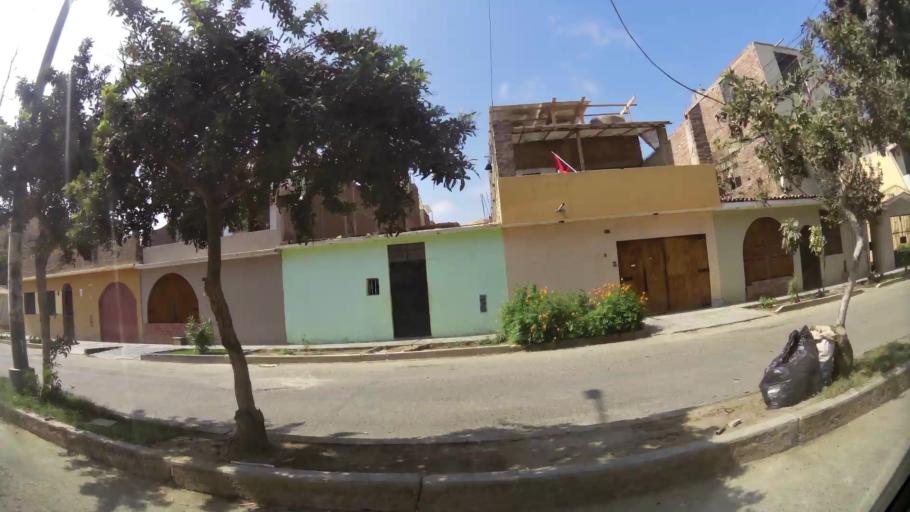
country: PE
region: La Libertad
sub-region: Provincia de Trujillo
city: Buenos Aires
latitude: -8.1305
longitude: -79.0488
